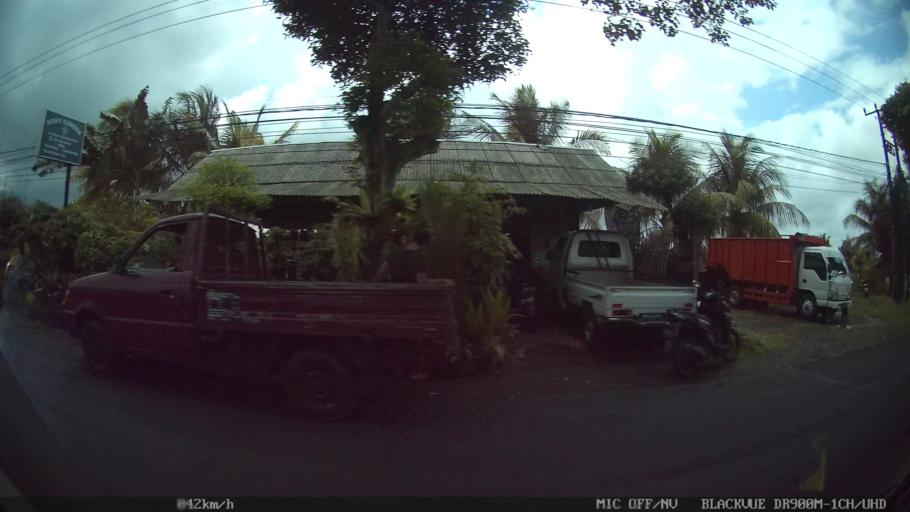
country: ID
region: Bali
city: Banjar Keraman
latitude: -8.5400
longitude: 115.2143
